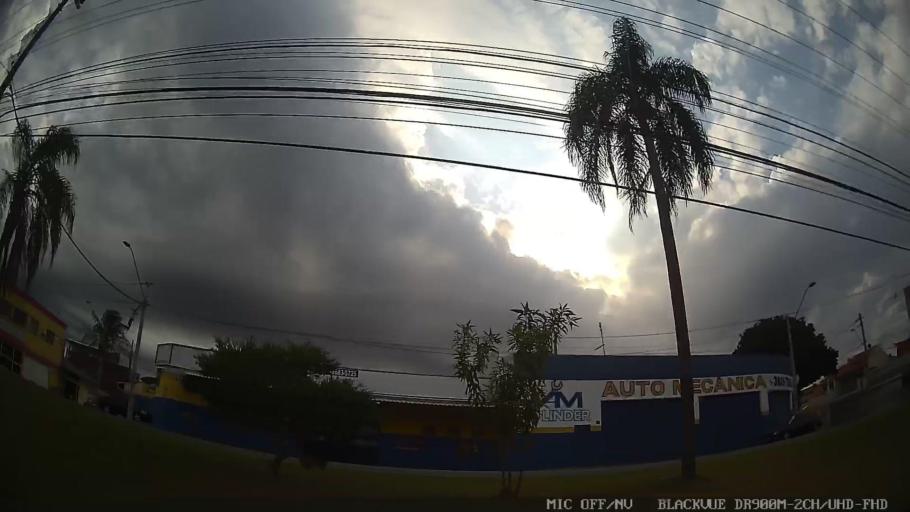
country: BR
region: Sao Paulo
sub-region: Indaiatuba
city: Indaiatuba
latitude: -23.1176
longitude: -47.2233
